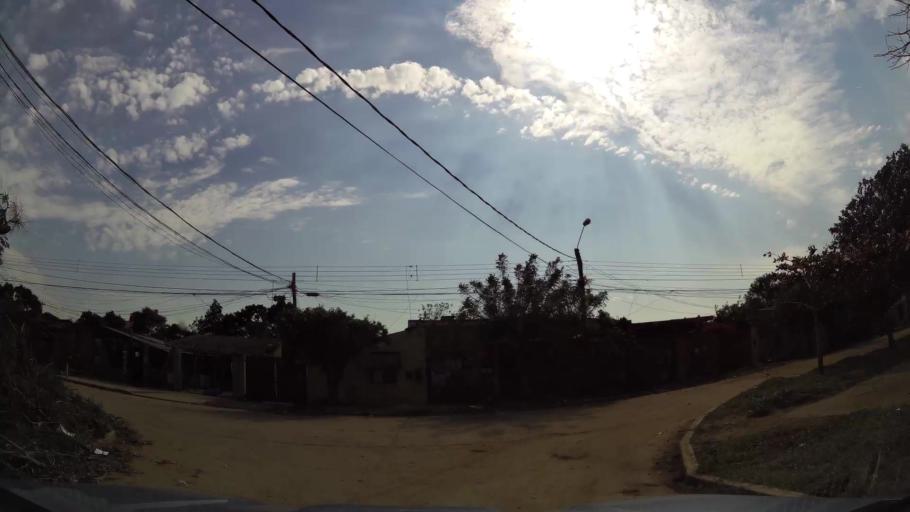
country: BO
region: Santa Cruz
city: Santa Cruz de la Sierra
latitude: -17.7273
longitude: -63.1547
